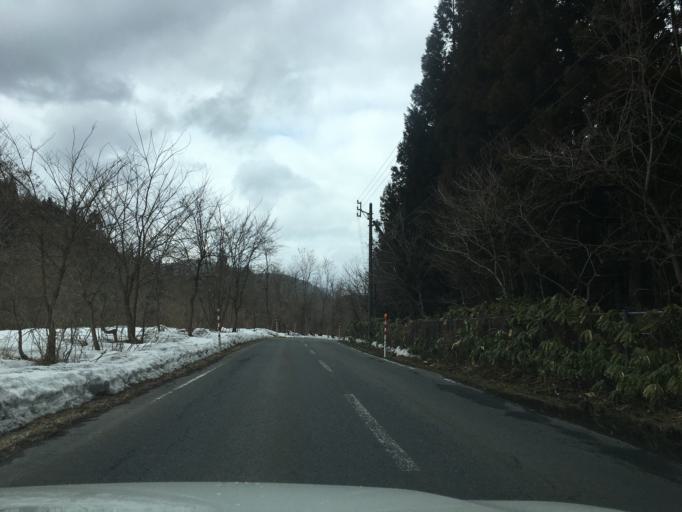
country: JP
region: Akita
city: Odate
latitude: 40.4323
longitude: 140.6436
